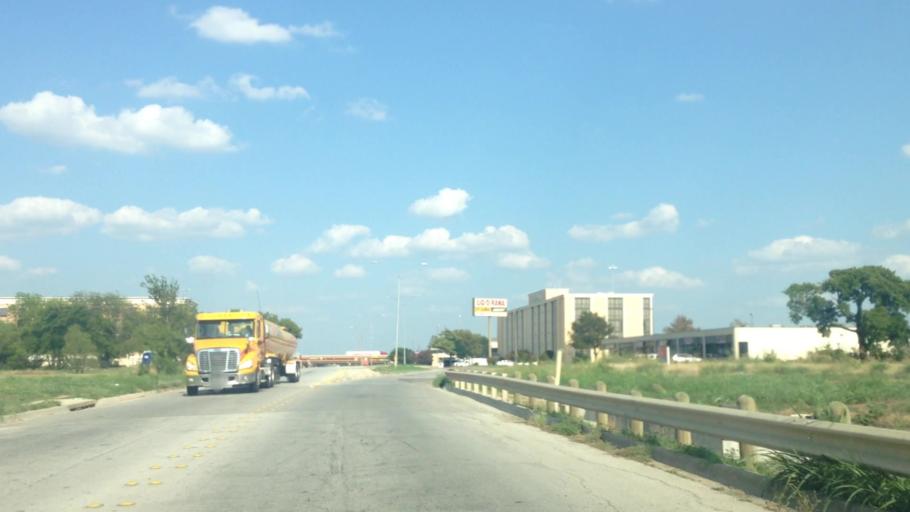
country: US
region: Texas
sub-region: Tarrant County
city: Blue Mound
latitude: 32.8245
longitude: -97.3181
